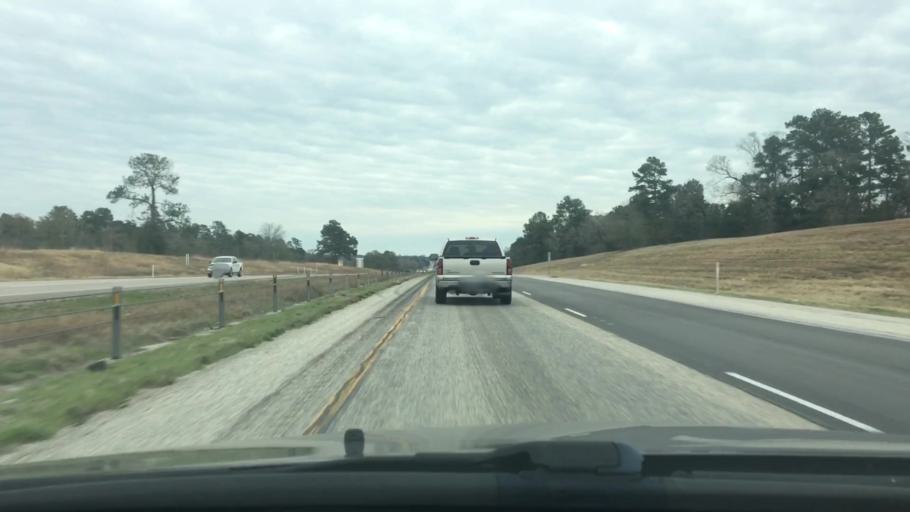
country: US
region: Texas
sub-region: Walker County
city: Huntsville
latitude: 30.7749
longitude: -95.6478
